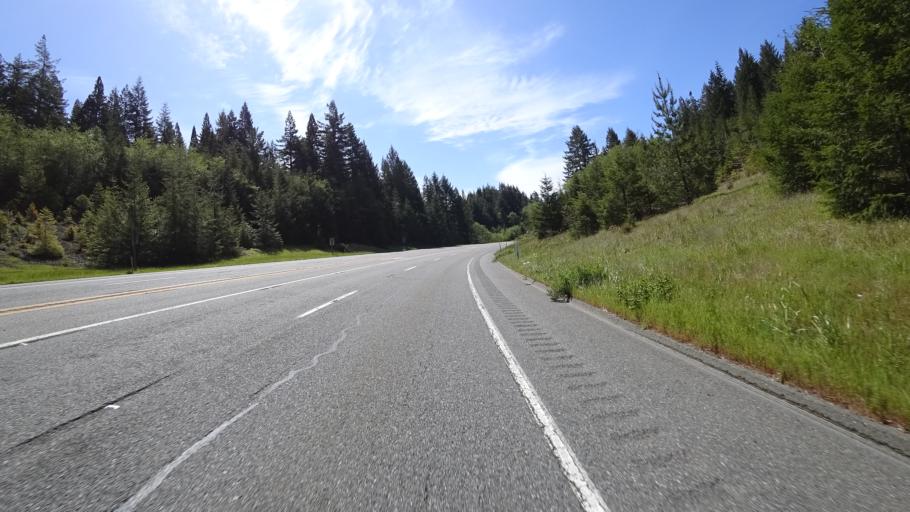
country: US
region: California
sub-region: Del Norte County
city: Bertsch-Oceanview
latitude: 41.4453
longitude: -124.0204
